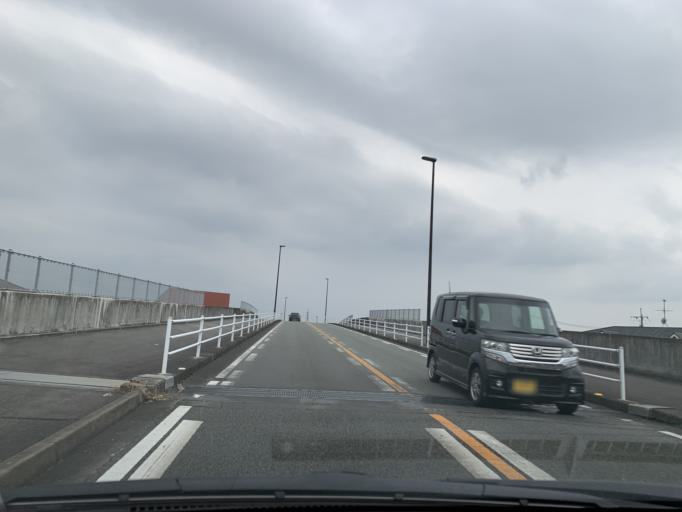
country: JP
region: Kumamoto
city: Ozu
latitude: 32.8777
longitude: 130.8762
